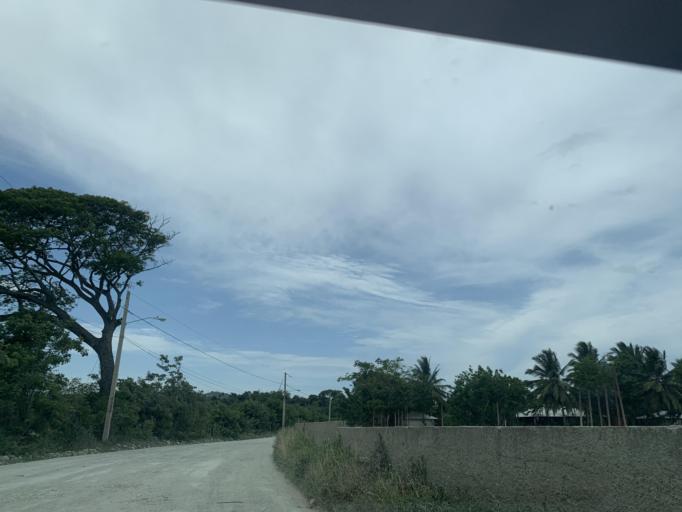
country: DO
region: Puerto Plata
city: Imbert
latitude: 19.8222
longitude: -70.7837
